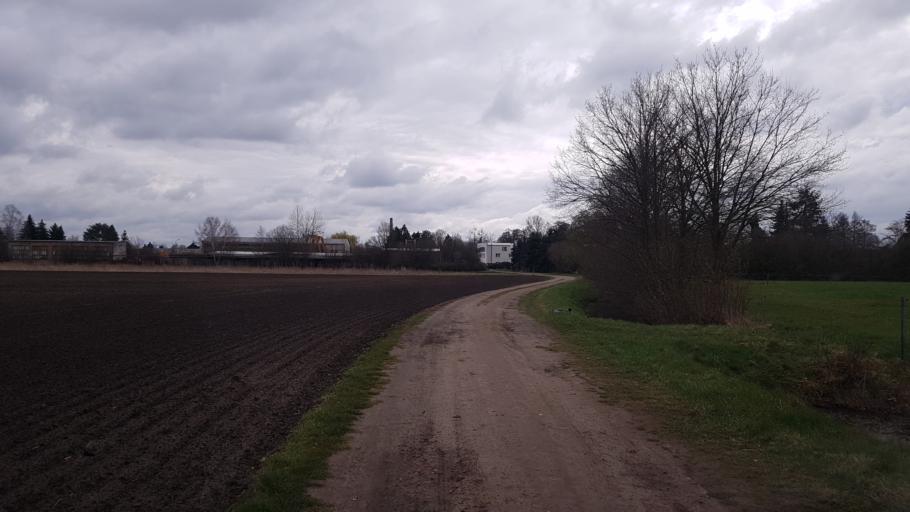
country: DE
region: Brandenburg
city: Doberlug-Kirchhain
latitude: 51.6458
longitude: 13.5624
